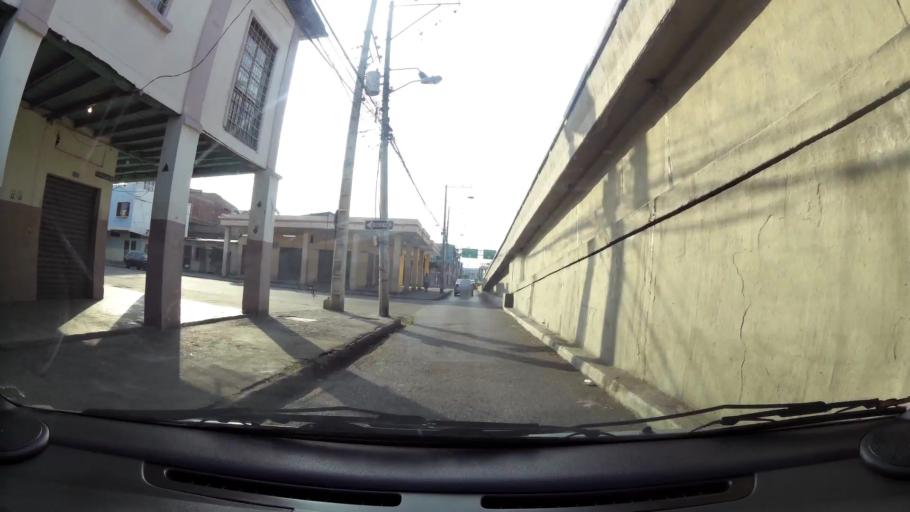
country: EC
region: Guayas
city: Guayaquil
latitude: -2.1852
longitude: -79.8872
